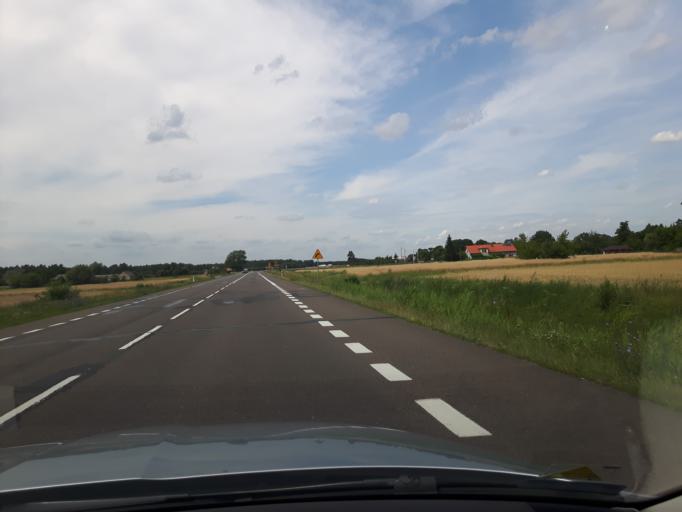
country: PL
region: Masovian Voivodeship
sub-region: Powiat ciechanowski
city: Glinojeck
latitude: 52.7895
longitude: 20.2779
